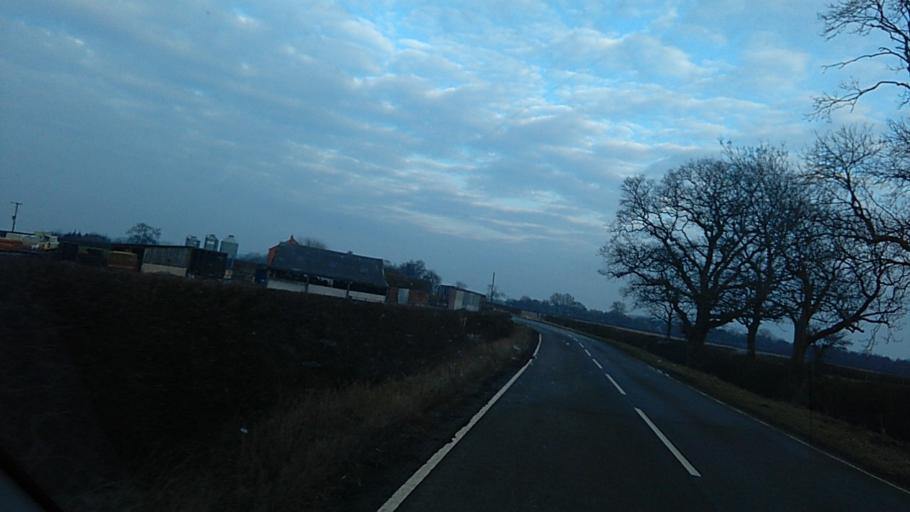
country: GB
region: England
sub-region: Leicestershire
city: Melton Mowbray
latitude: 52.8272
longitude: -0.9002
